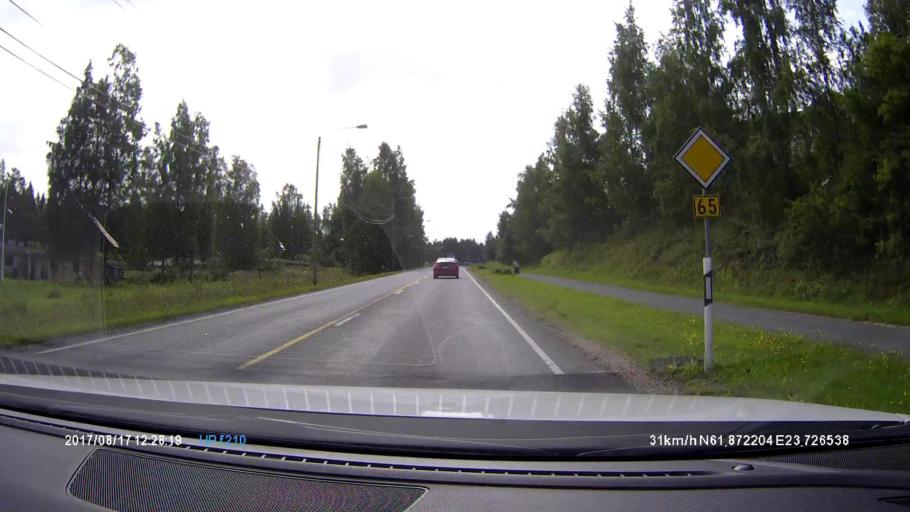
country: FI
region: Pirkanmaa
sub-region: Tampere
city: Kuru
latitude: 61.8720
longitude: 23.7266
